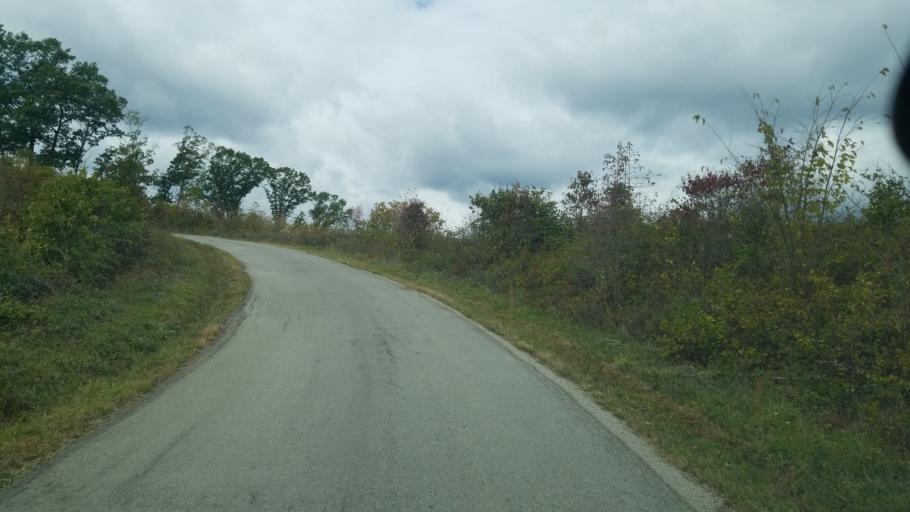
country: US
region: Ohio
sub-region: Jackson County
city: Wellston
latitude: 39.1609
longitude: -82.5847
